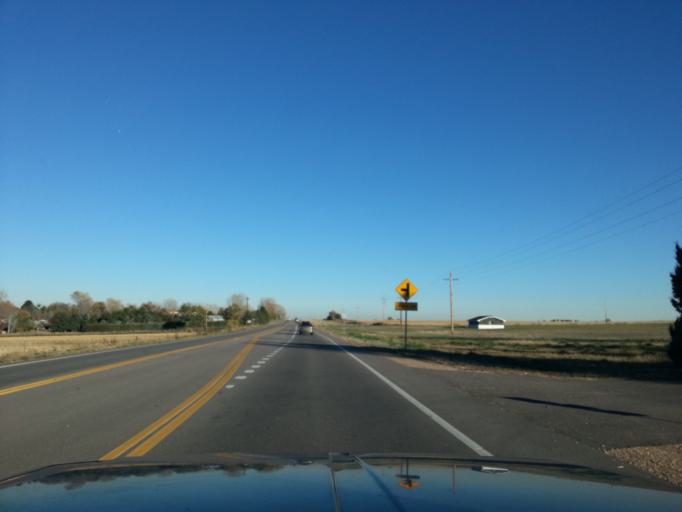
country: US
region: Colorado
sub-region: Larimer County
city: Loveland
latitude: 40.3782
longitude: -105.0147
